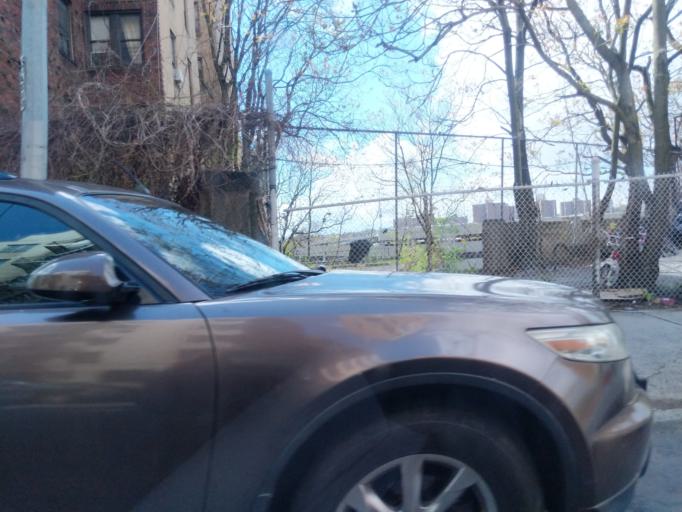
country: US
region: New York
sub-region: New York County
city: Inwood
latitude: 40.8241
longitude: -73.9271
